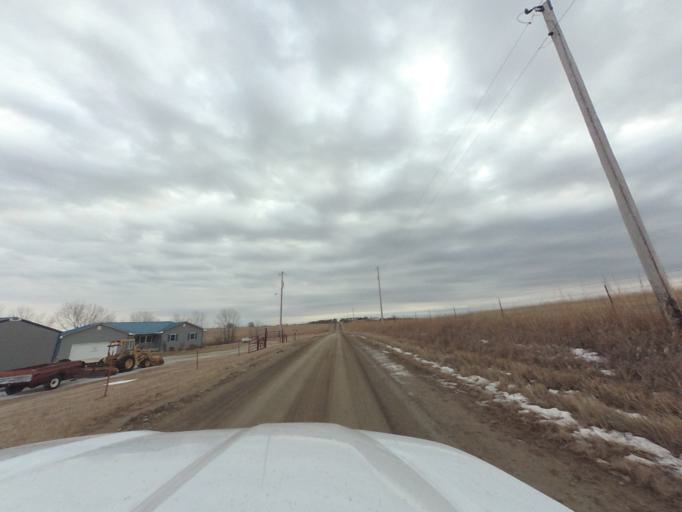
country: US
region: Kansas
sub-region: Chase County
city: Cottonwood Falls
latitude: 38.4492
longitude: -96.3848
